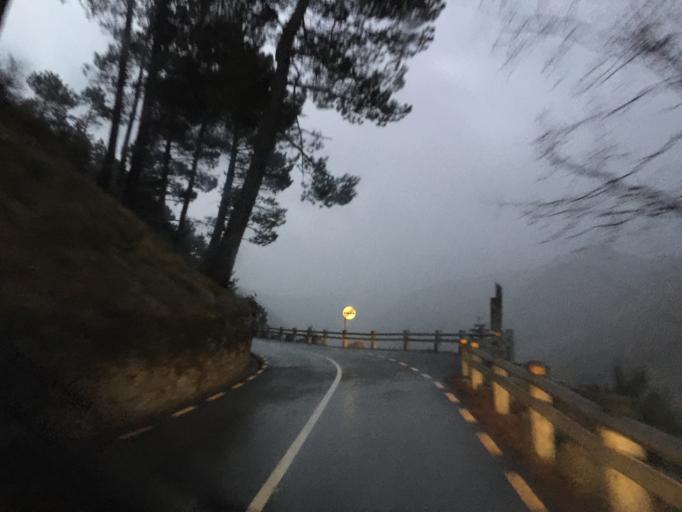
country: PT
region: Guarda
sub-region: Manteigas
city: Manteigas
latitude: 40.3507
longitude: -7.5599
